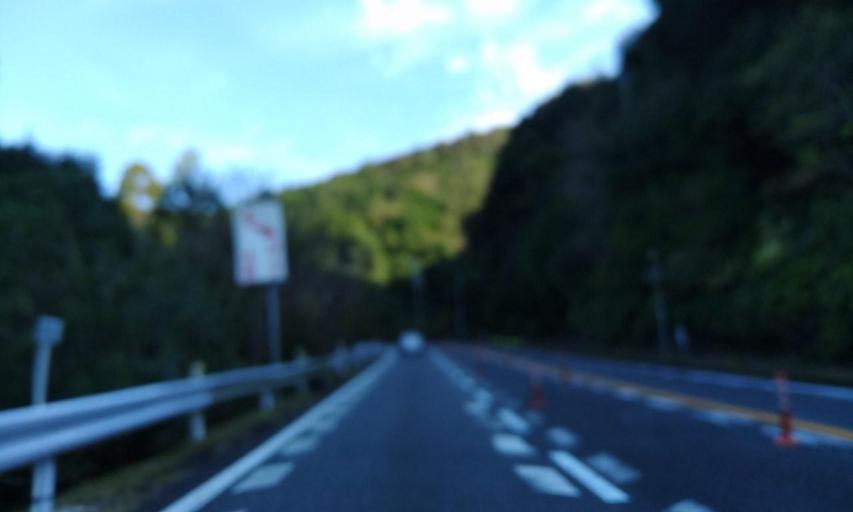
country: JP
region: Mie
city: Ise
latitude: 34.4063
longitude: 136.7692
